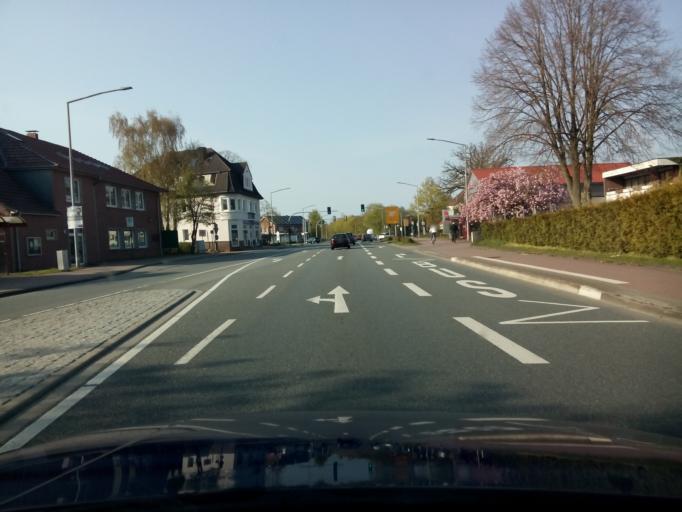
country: DE
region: Lower Saxony
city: Syke
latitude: 52.9386
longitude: 8.8261
